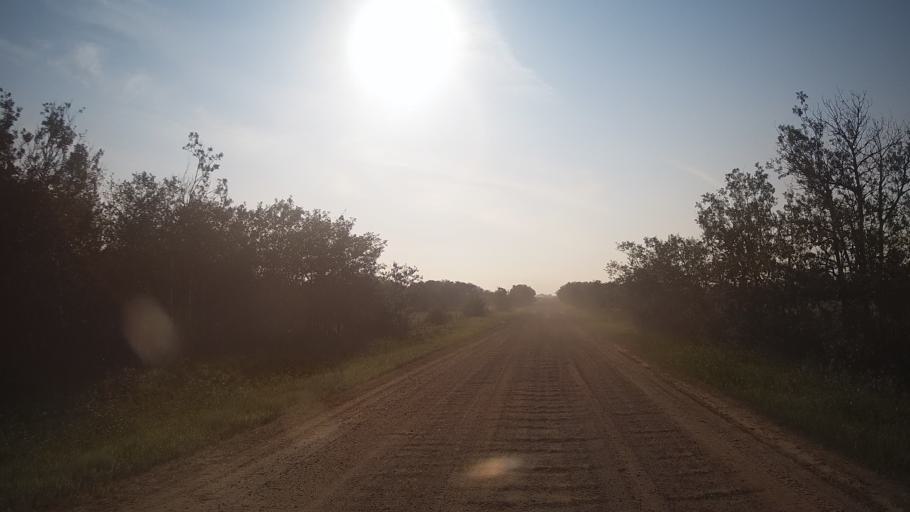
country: CA
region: Saskatchewan
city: Saskatoon
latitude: 51.8237
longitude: -106.5352
